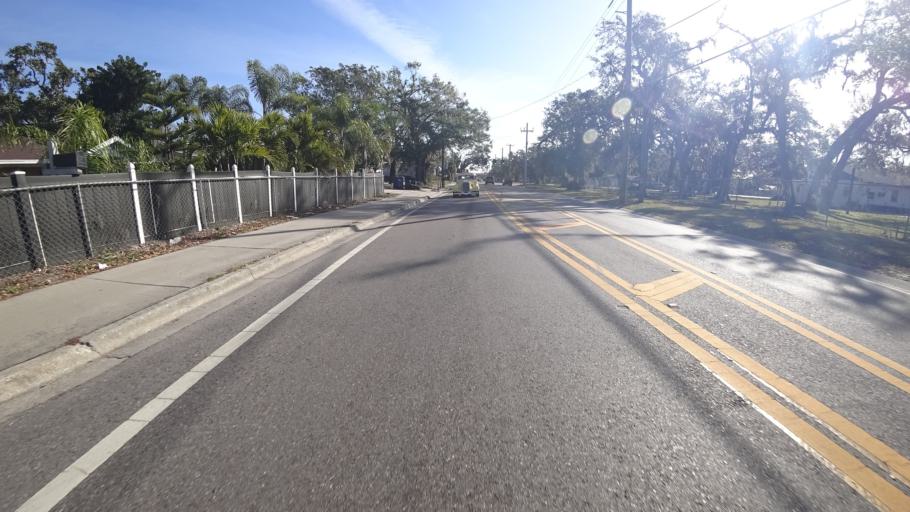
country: US
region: Florida
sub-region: Manatee County
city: West Samoset
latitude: 27.4770
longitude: -82.5557
